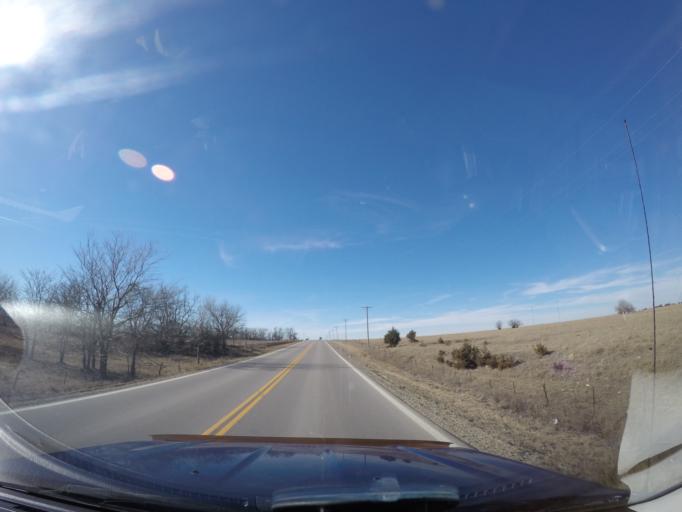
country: US
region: Kansas
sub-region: Dickinson County
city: Herington
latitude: 38.6674
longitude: -96.8999
